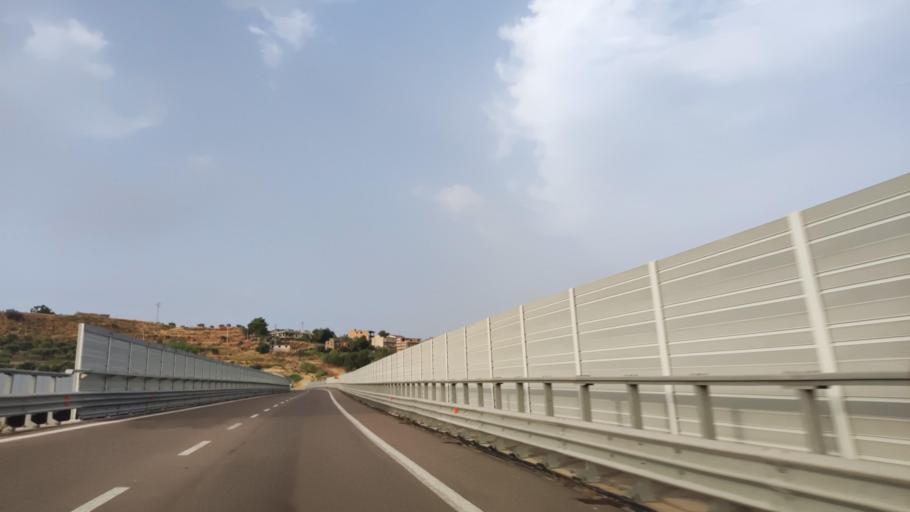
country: IT
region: Calabria
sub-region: Provincia di Reggio Calabria
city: Siderno
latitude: 38.2919
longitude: 16.2826
